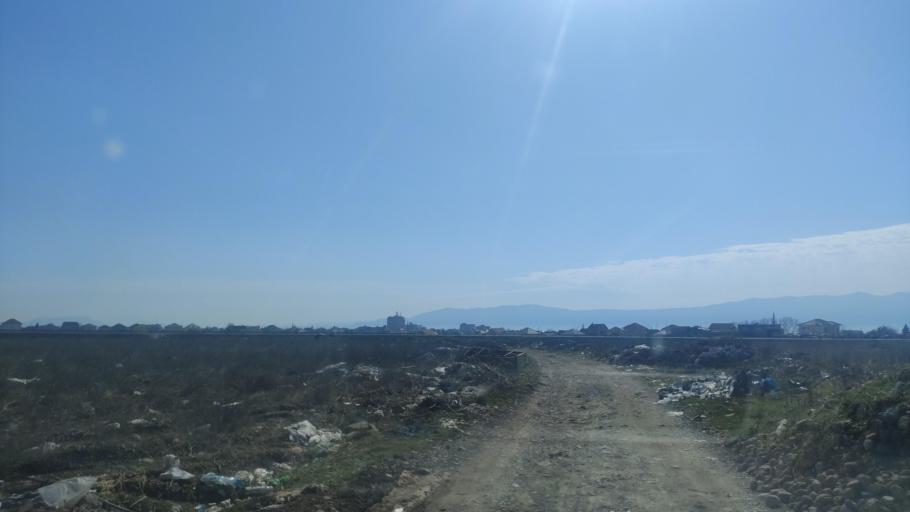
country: AL
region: Shkoder
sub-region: Rrethi i Malesia e Madhe
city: Koplik
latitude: 42.2243
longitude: 19.4346
